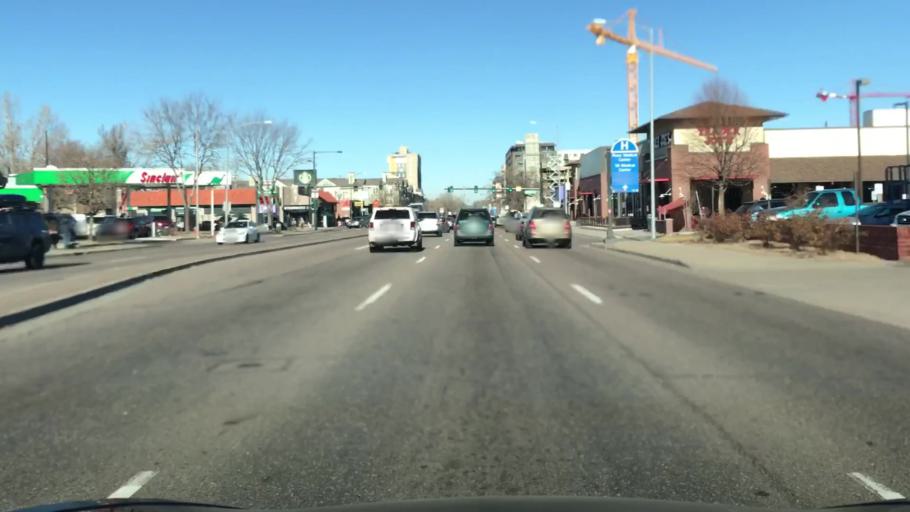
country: US
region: Colorado
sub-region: Arapahoe County
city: Glendale
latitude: 39.7280
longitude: -104.9407
